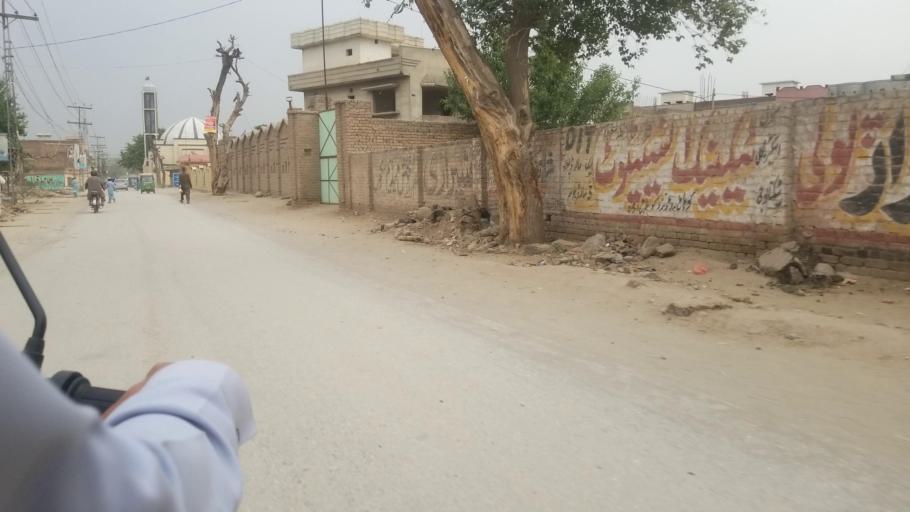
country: PK
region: Khyber Pakhtunkhwa
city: Peshawar
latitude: 33.9849
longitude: 71.5551
